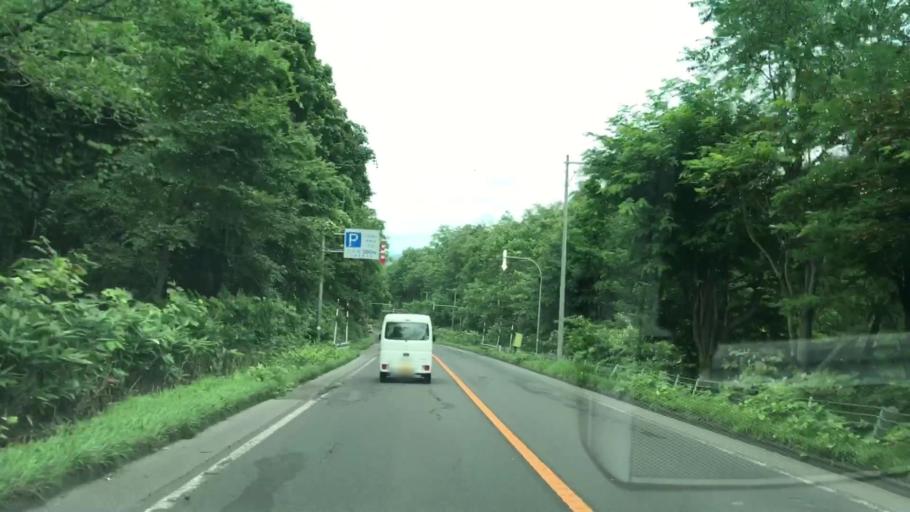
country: JP
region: Hokkaido
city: Niseko Town
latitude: 42.9471
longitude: 140.7035
